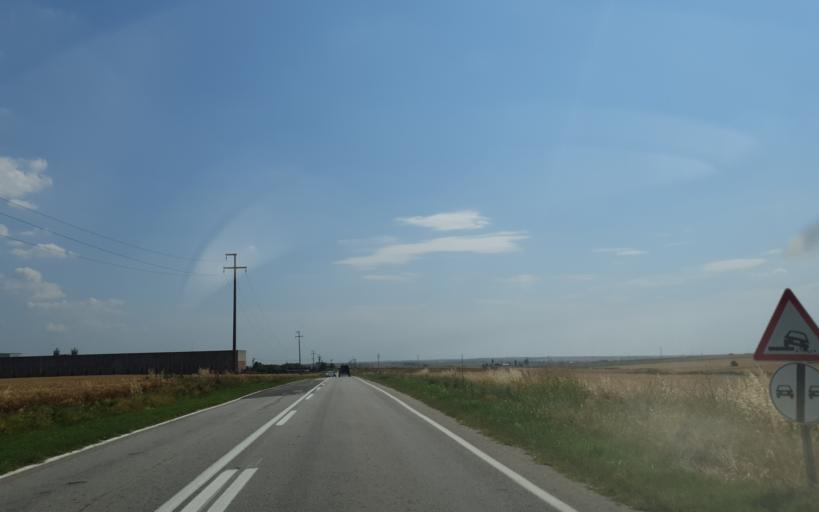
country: TR
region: Kirklareli
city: Buyukkaristiran
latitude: 41.3217
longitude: 27.5246
